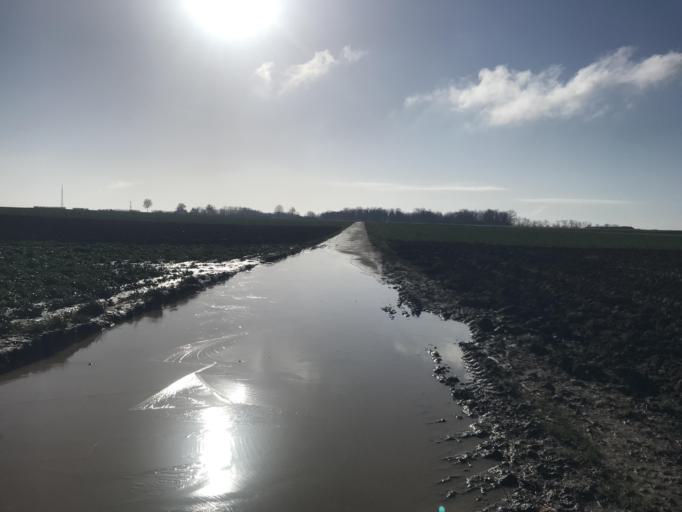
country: DE
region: Rheinland-Pfalz
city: Ober-Hilbersheim
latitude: 49.8888
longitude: 8.0270
